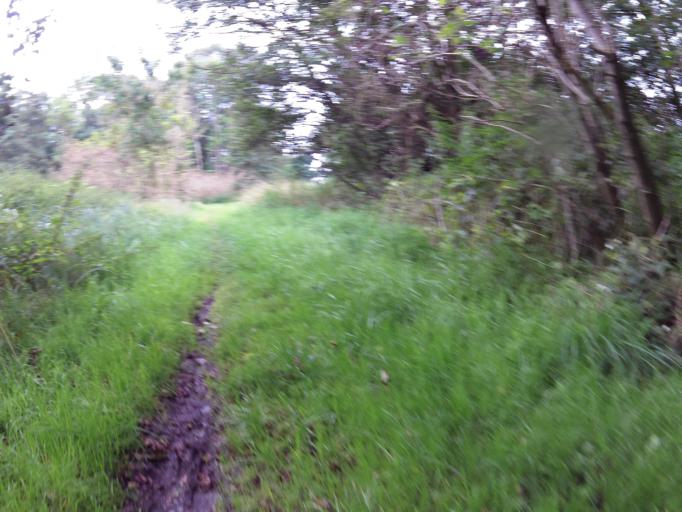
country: DE
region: Schleswig-Holstein
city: Krummbek
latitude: 54.4167
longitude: 10.3961
